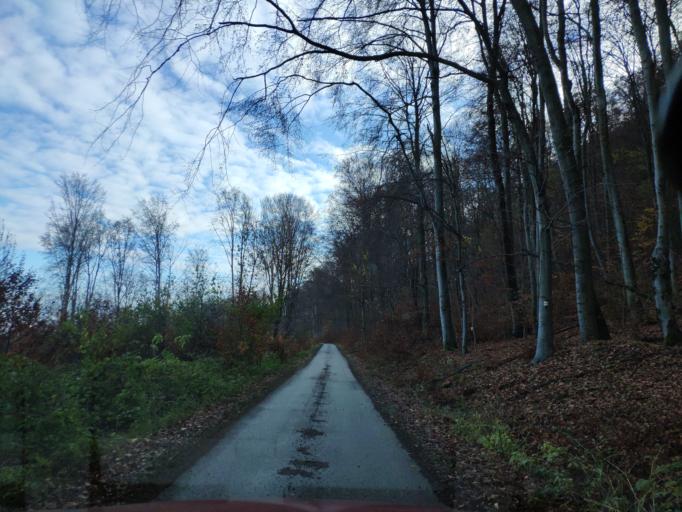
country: HU
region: Borsod-Abauj-Zemplen
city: Gonc
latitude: 48.5859
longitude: 21.4690
